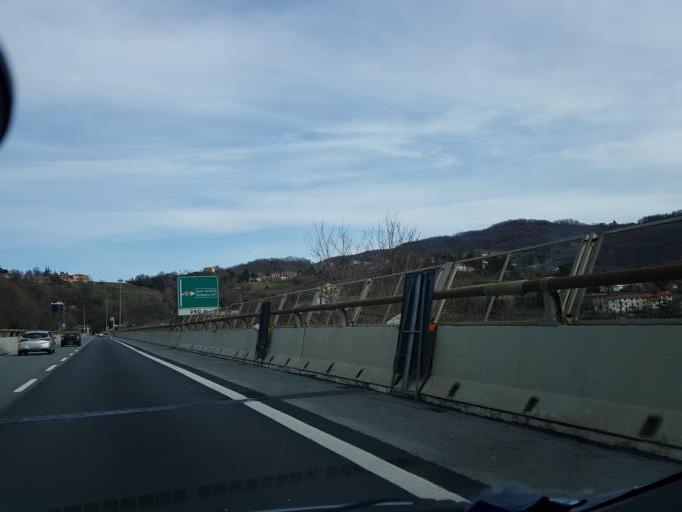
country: IT
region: Liguria
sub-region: Provincia di Genova
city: Serra Ricco
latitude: 44.5266
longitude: 8.9384
